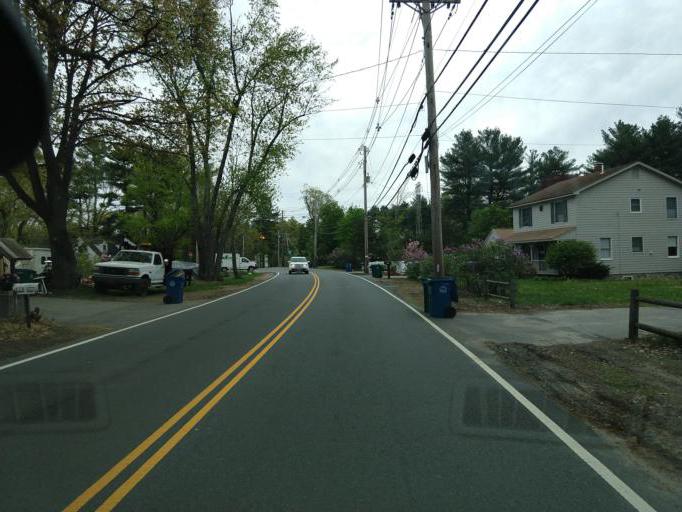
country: US
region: Massachusetts
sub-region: Middlesex County
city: Billerica
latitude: 42.5743
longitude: -71.2402
